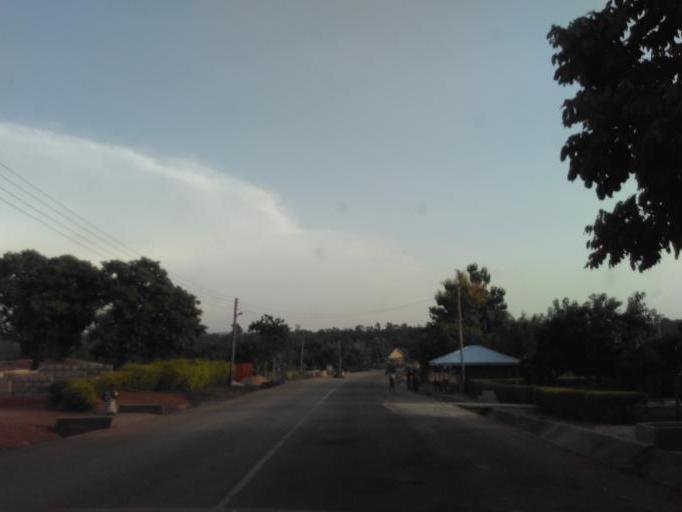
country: GH
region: Ashanti
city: Mamponteng
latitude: 6.6273
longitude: -1.4500
